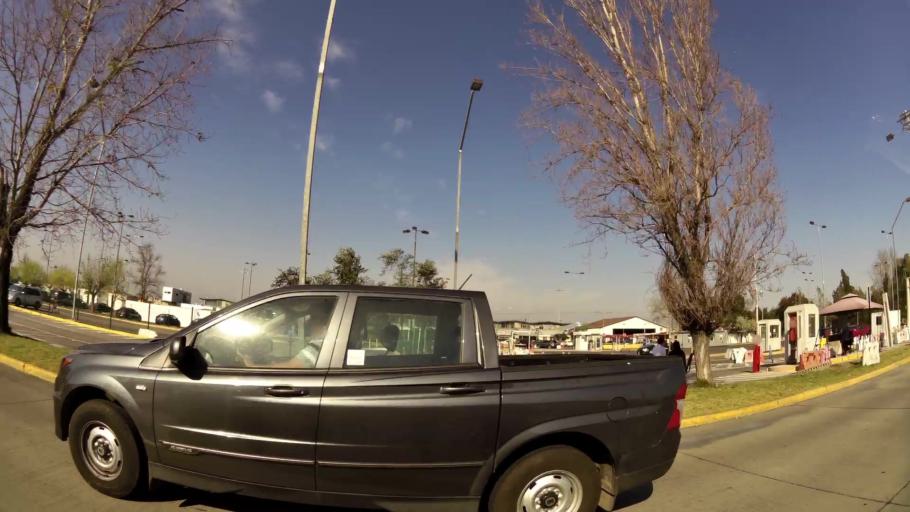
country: CL
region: Santiago Metropolitan
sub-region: Provincia de Santiago
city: Lo Prado
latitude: -33.3991
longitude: -70.7922
